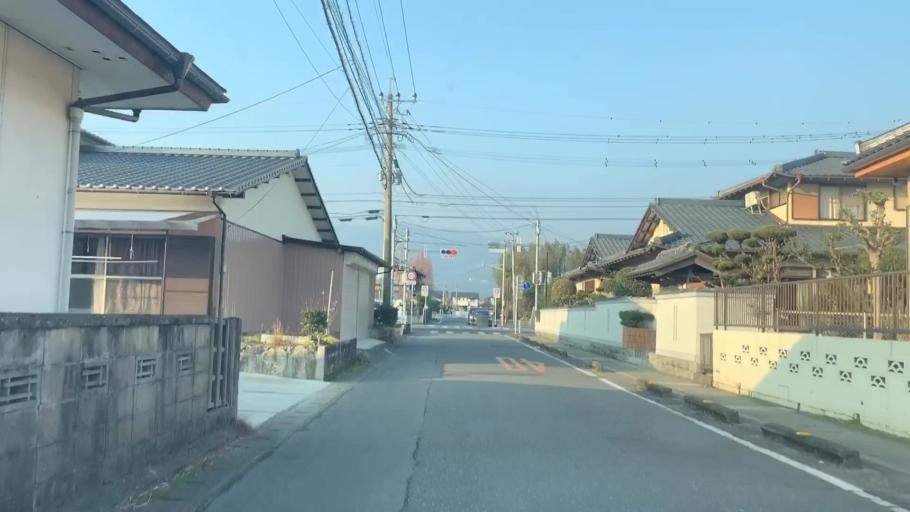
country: JP
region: Saga Prefecture
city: Saga-shi
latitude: 33.2794
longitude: 130.2261
